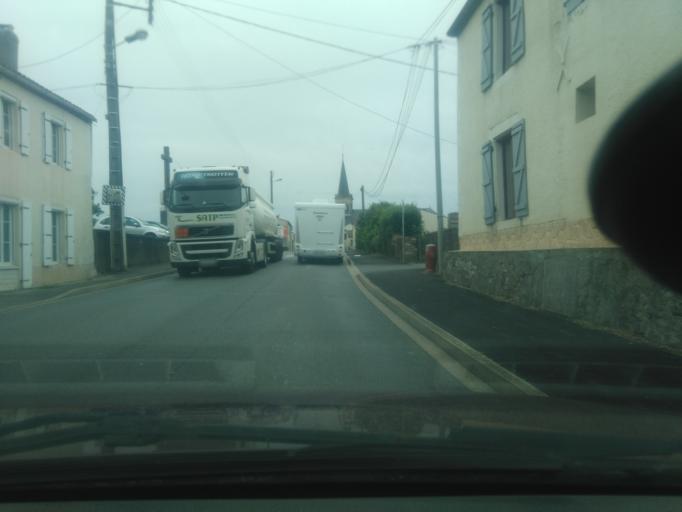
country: FR
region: Pays de la Loire
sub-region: Departement de la Vendee
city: Sainte-Cecile
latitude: 46.7420
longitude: -1.0875
